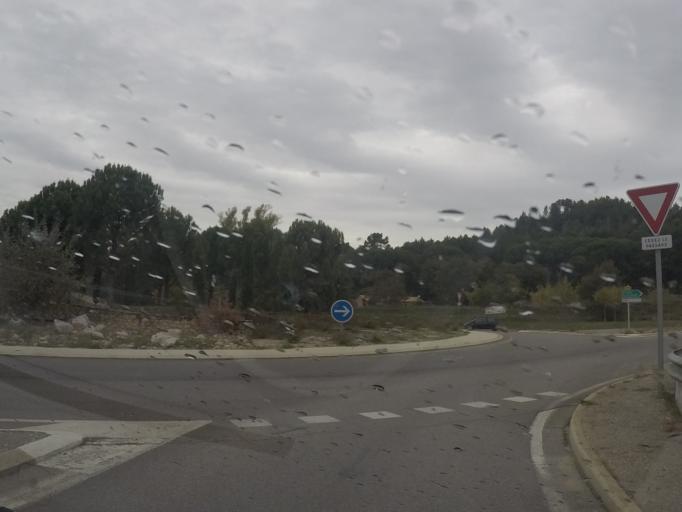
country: FR
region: Provence-Alpes-Cote d'Azur
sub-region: Departement du Vaucluse
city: Goult
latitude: 43.8588
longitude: 5.2667
